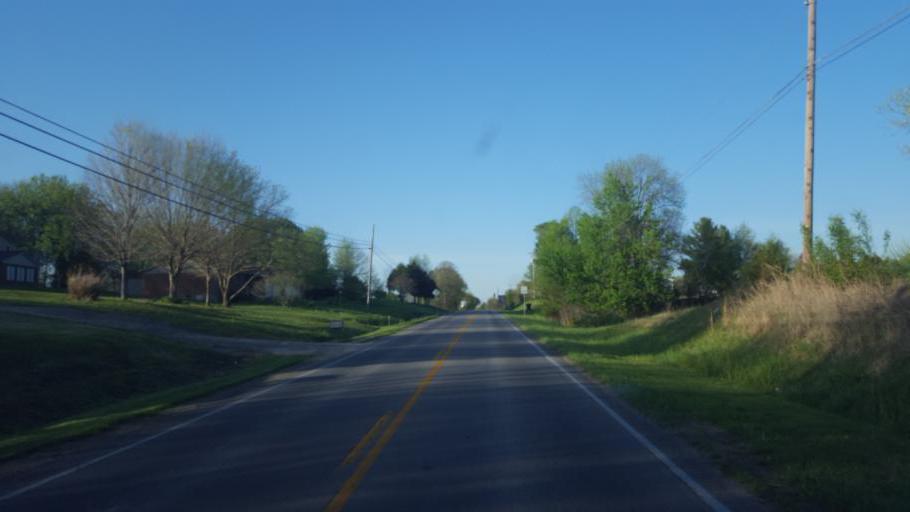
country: US
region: Kentucky
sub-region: Hart County
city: Munfordville
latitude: 37.2554
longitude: -85.8865
